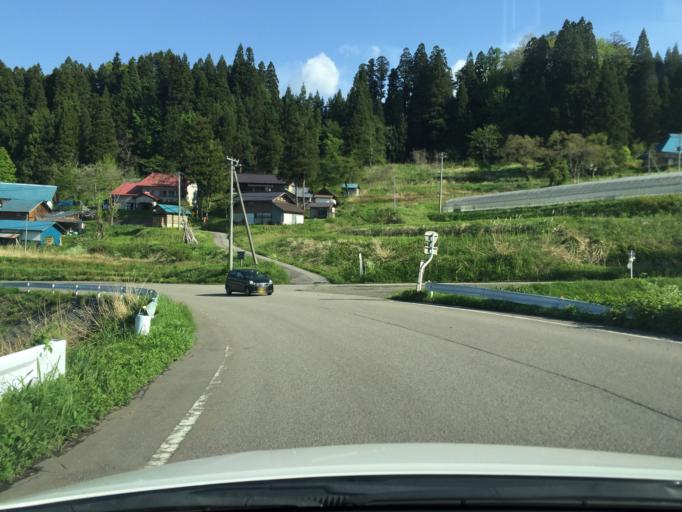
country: JP
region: Fukushima
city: Kitakata
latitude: 37.6829
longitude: 139.6821
